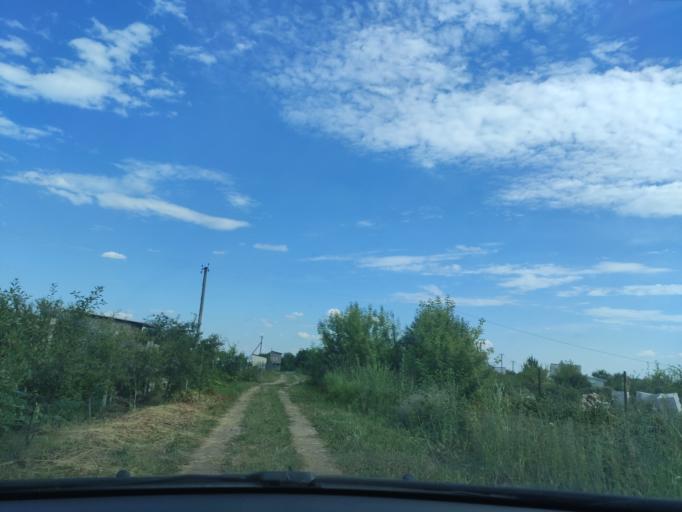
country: RU
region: Ulyanovsk
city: Cherdakly
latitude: 54.4430
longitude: 48.8958
